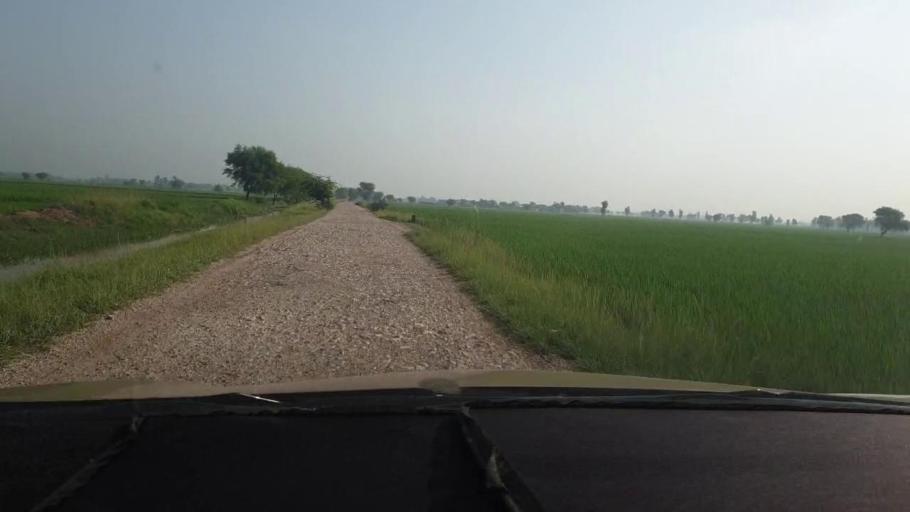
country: PK
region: Sindh
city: Kambar
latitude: 27.5887
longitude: 68.1039
